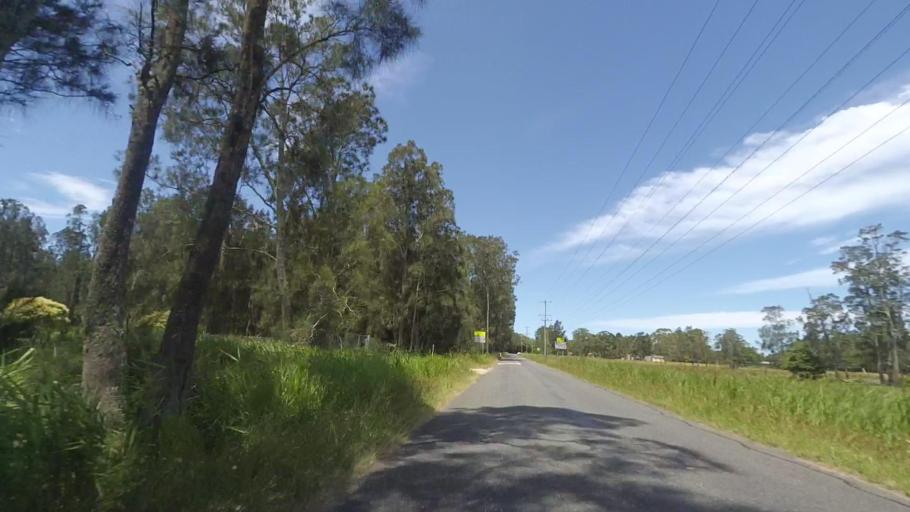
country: AU
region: New South Wales
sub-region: Port Stephens Shire
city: Port Stephens
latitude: -32.7666
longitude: 152.0071
